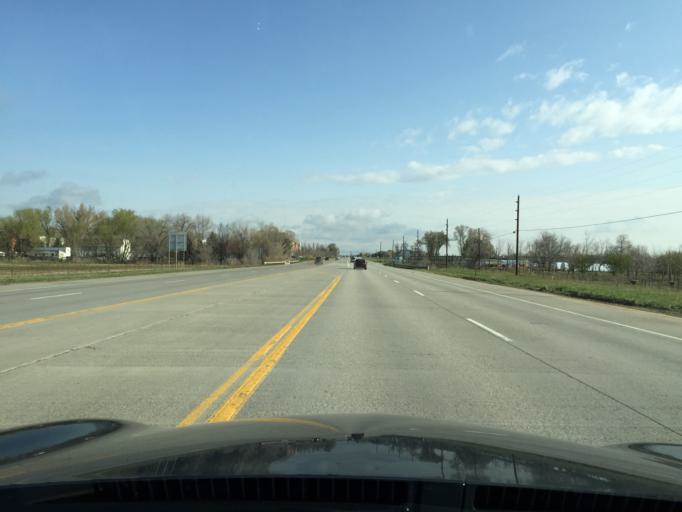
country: US
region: Colorado
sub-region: Boulder County
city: Longmont
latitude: 40.1310
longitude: -105.1025
